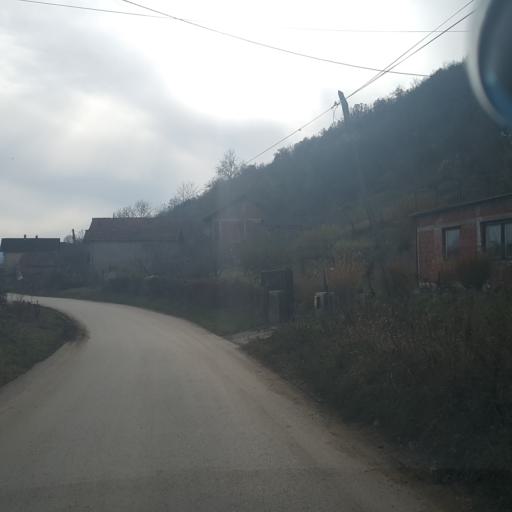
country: RS
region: Central Serbia
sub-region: Zajecarski Okrug
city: Knjazevac
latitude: 43.5944
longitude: 22.2537
